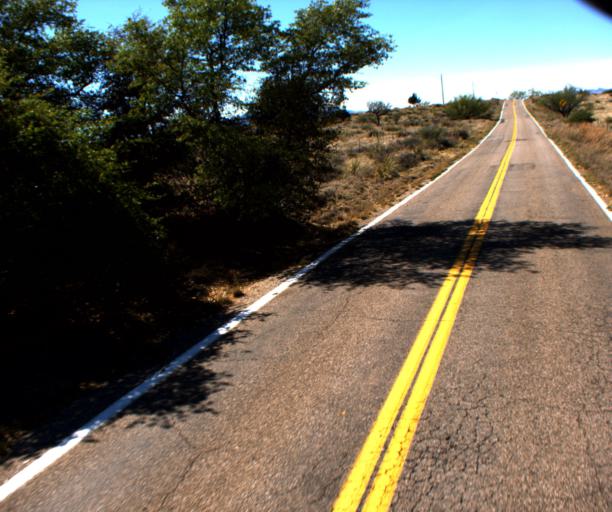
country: US
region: Arizona
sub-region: Cochise County
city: Huachuca City
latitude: 31.5839
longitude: -110.5609
